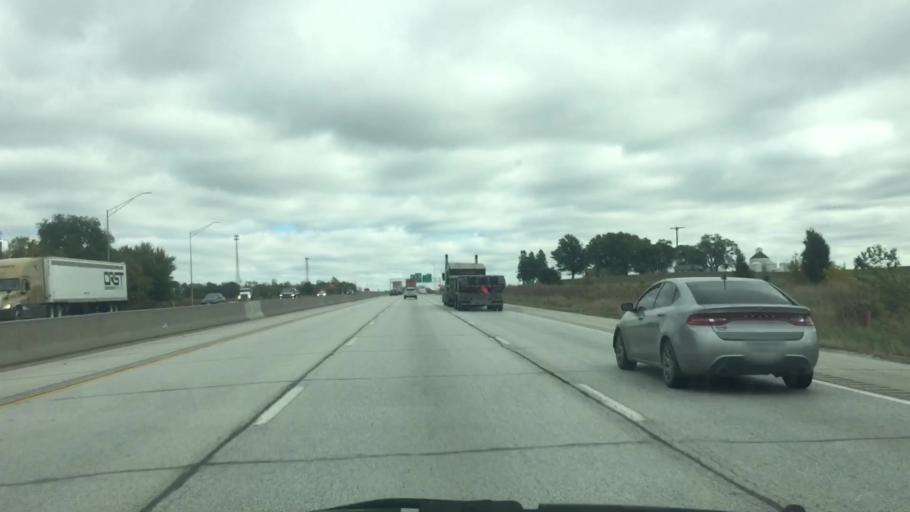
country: US
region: Iowa
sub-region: Polk County
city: Altoona
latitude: 41.6583
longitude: -93.5333
